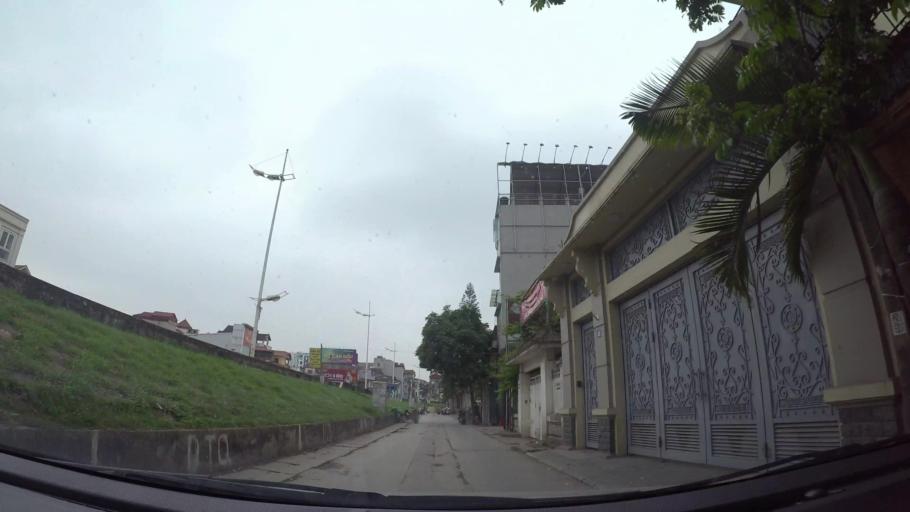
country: VN
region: Ha Noi
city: Tay Ho
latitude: 21.0614
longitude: 105.8341
